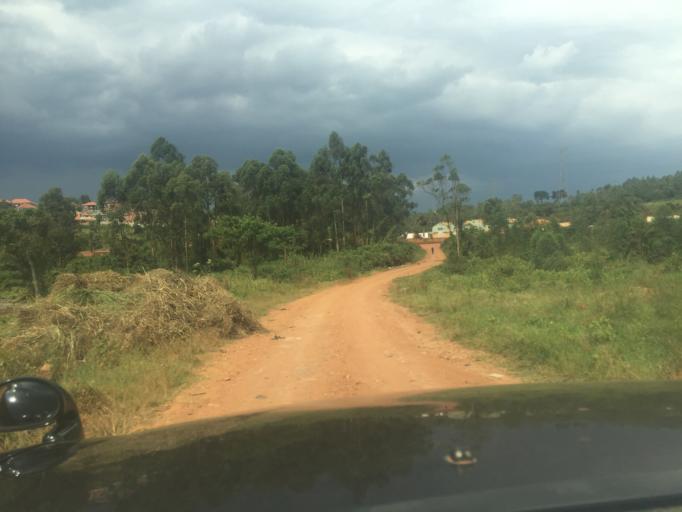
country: UG
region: Central Region
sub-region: Wakiso District
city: Kireka
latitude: 0.4075
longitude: 32.6280
